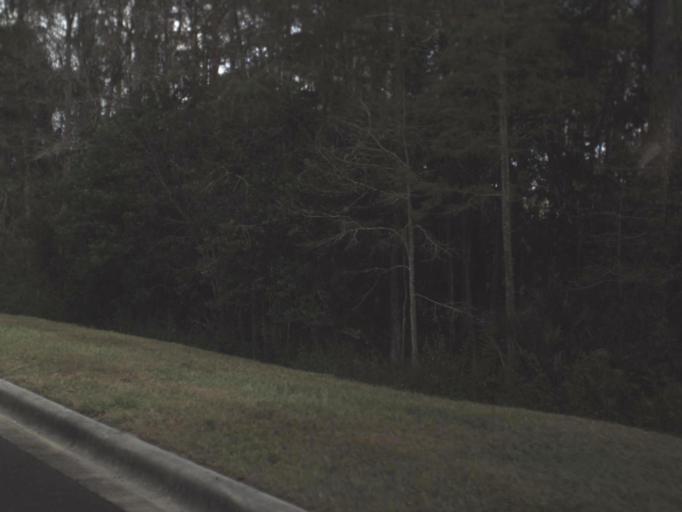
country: US
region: Florida
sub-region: Osceola County
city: Celebration
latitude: 28.3386
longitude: -81.4981
